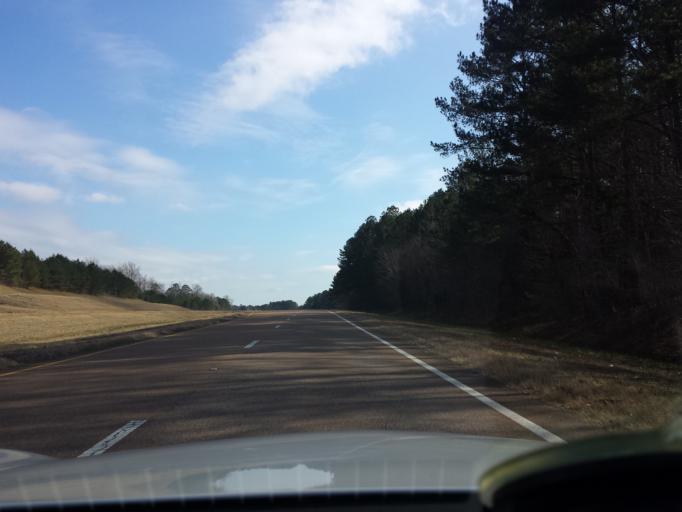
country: US
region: Mississippi
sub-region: Winston County
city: Louisville
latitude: 33.1714
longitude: -89.0533
